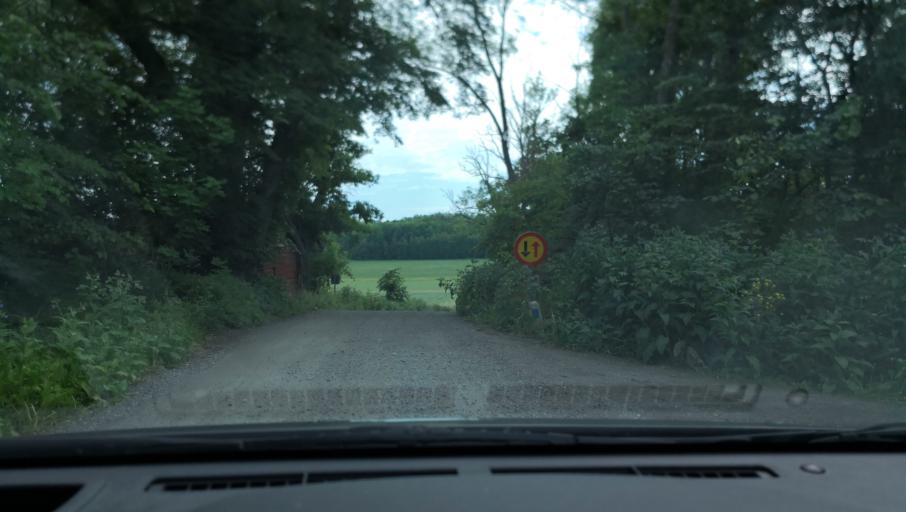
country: SE
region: Uppsala
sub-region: Uppsala Kommun
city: Uppsala
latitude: 59.8067
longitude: 17.5338
